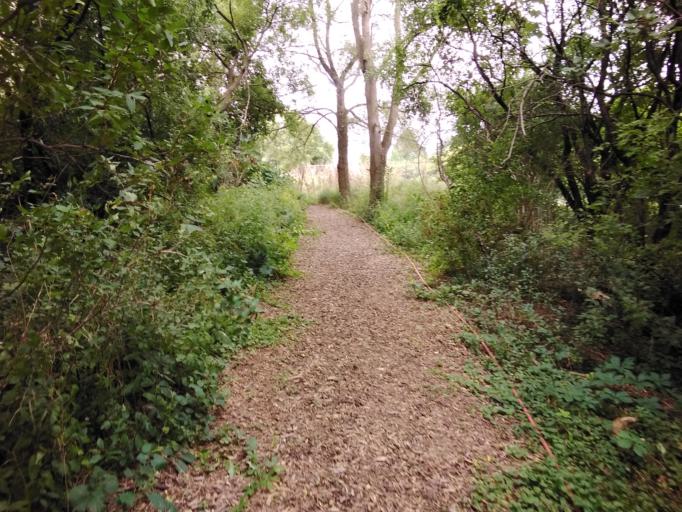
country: US
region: Wisconsin
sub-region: Milwaukee County
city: Brown Deer
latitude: 43.1750
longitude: -88.0052
